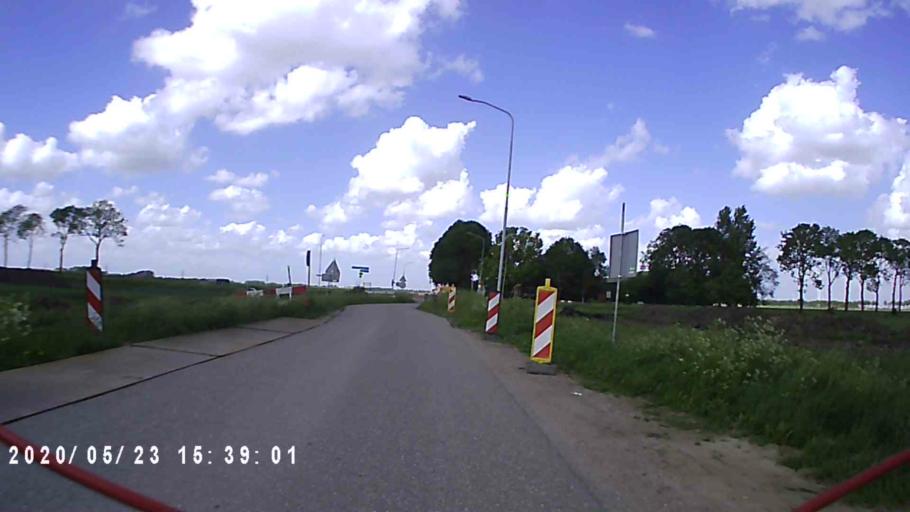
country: NL
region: Groningen
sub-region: Gemeente Delfzijl
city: Delfzijl
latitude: 53.2798
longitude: 6.9408
